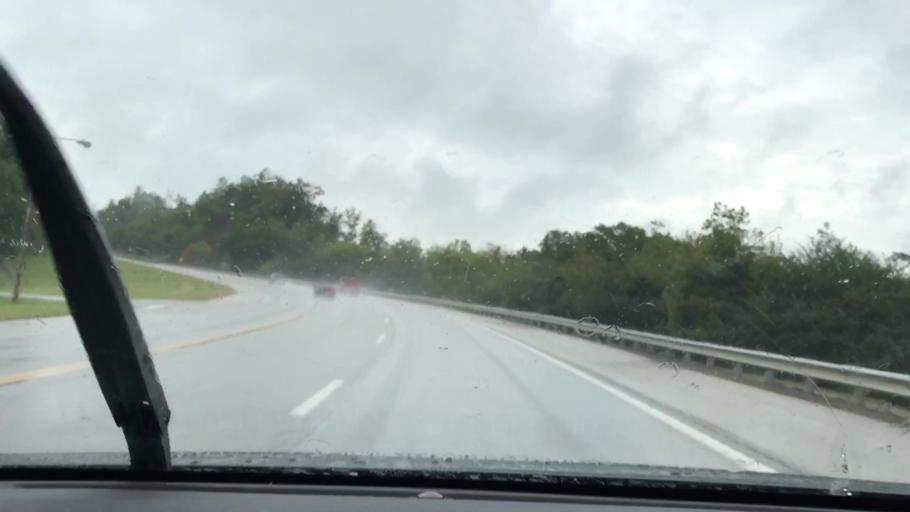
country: US
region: Tennessee
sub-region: Scott County
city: Huntsville
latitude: 36.3834
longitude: -84.5440
